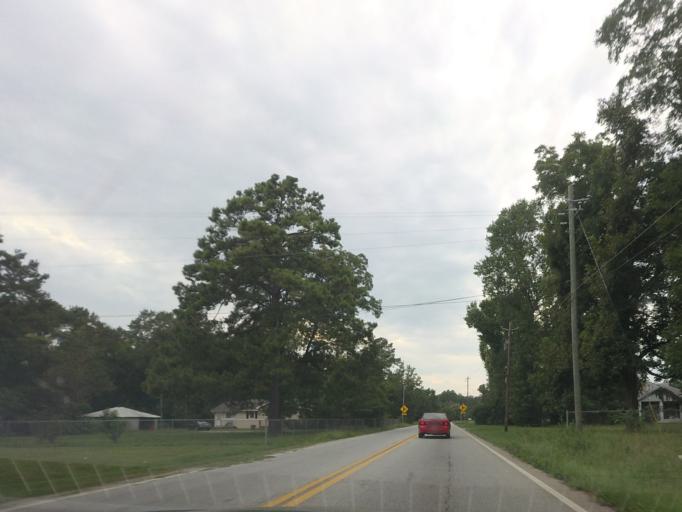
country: US
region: Georgia
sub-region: Bibb County
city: Macon
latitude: 32.8068
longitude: -83.5088
